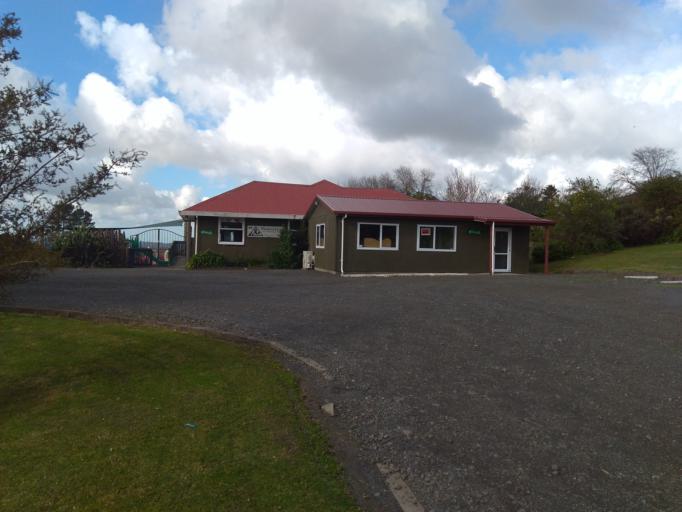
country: NZ
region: Auckland
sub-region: Auckland
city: Rosebank
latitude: -36.8295
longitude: 174.6099
